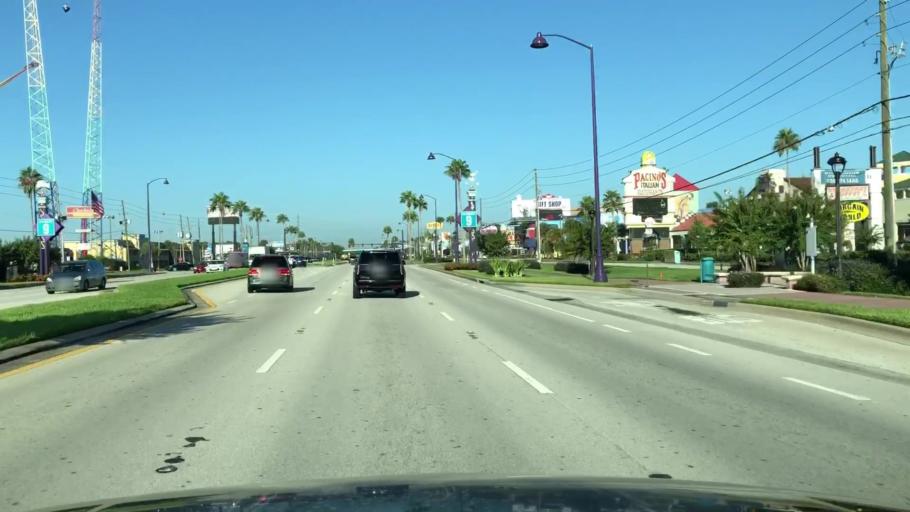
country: US
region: Florida
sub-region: Osceola County
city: Celebration
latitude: 28.3329
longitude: -81.5146
